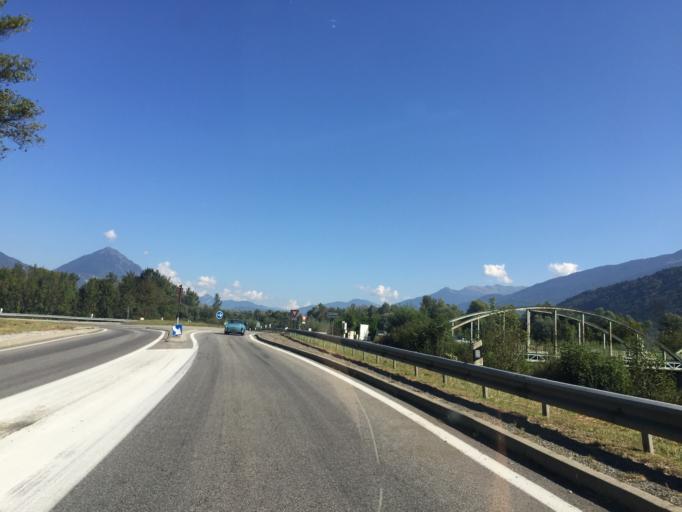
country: FR
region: Rhone-Alpes
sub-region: Departement de la Savoie
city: Gresy-sur-Isere
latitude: 45.5837
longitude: 6.2689
